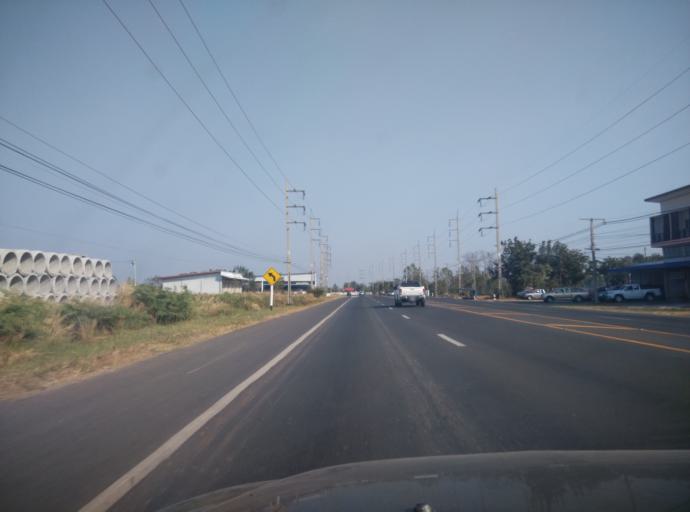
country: TH
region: Sisaket
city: Uthumphon Phisai
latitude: 15.1590
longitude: 104.1741
